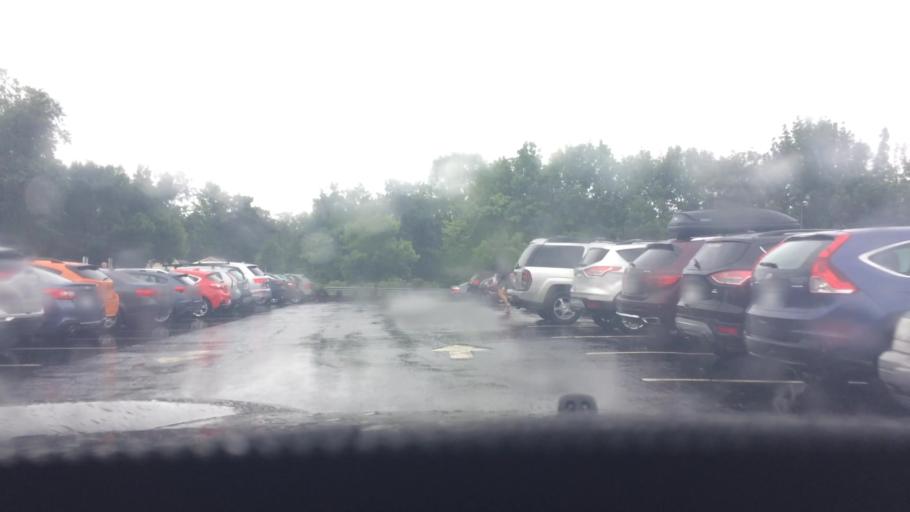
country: US
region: Massachusetts
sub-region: Worcester County
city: Charlton
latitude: 42.1398
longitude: -72.0257
